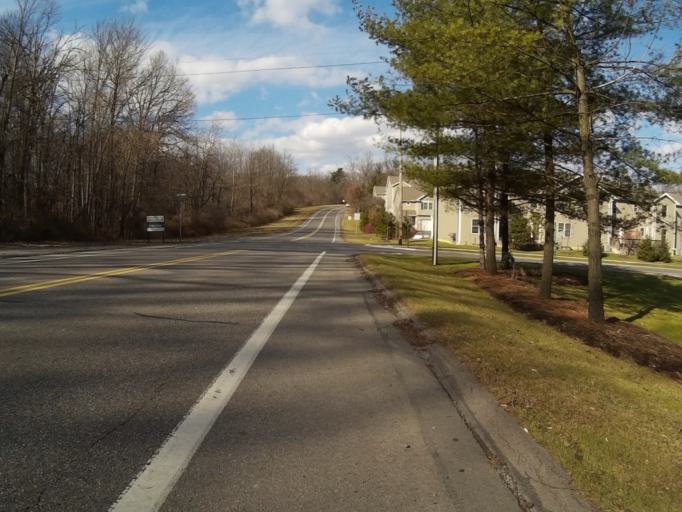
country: US
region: Pennsylvania
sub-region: Centre County
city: Park Forest Village
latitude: 40.8048
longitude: -77.9245
